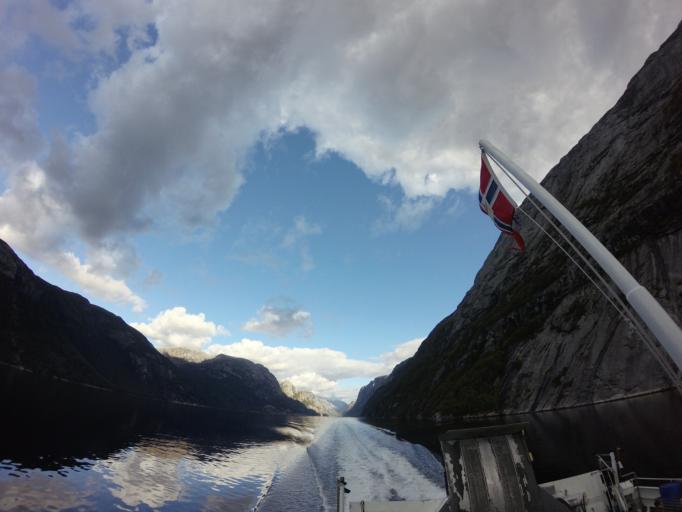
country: NO
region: Rogaland
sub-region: Hjelmeland
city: Hjelmelandsvagen
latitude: 59.0226
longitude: 6.4594
